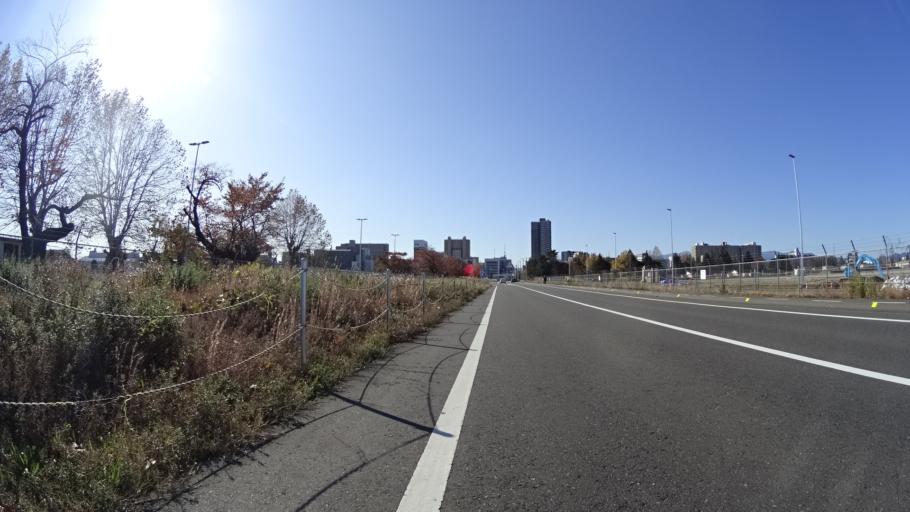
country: JP
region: Tokyo
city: Hachioji
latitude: 35.5850
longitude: 139.3750
